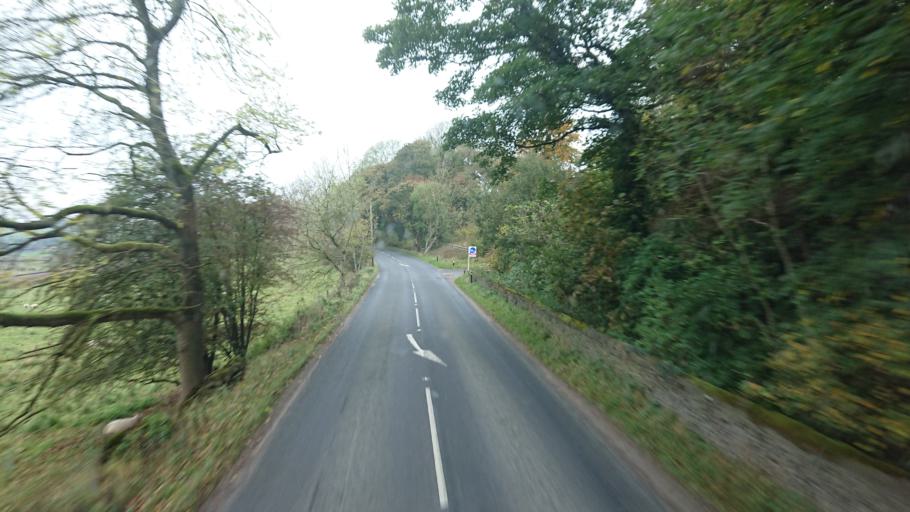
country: GB
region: England
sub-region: North Yorkshire
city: Skipton
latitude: 54.0067
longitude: -2.0475
